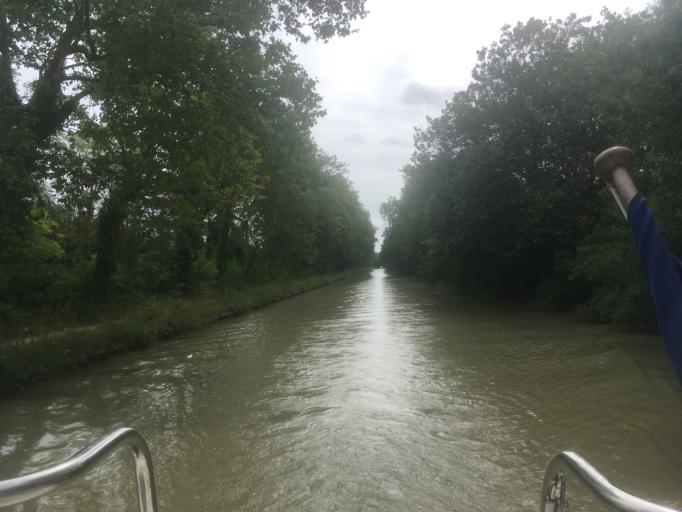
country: FR
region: Languedoc-Roussillon
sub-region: Departement de l'Aude
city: Villepinte
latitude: 43.2775
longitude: 2.0599
